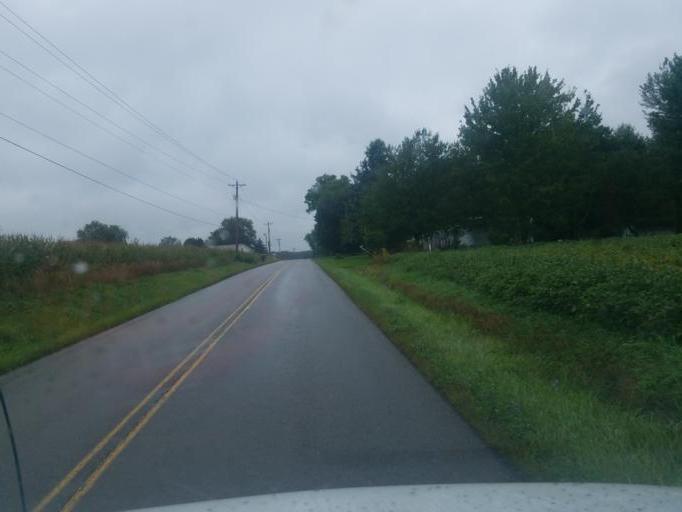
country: US
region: Ohio
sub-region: Medina County
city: Westfield Center
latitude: 40.9736
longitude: -81.9733
